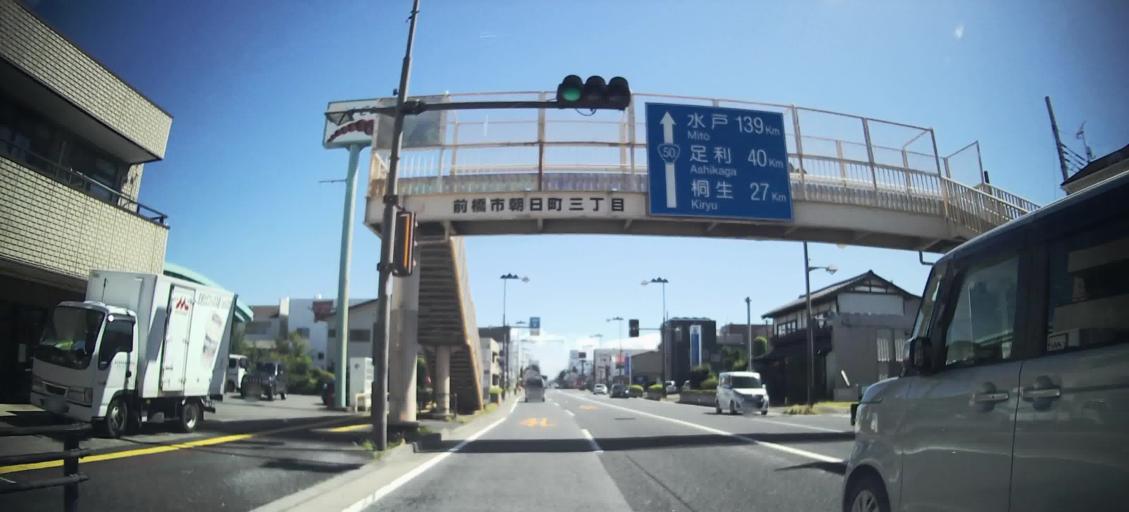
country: JP
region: Gunma
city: Maebashi-shi
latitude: 36.3843
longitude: 139.0859
